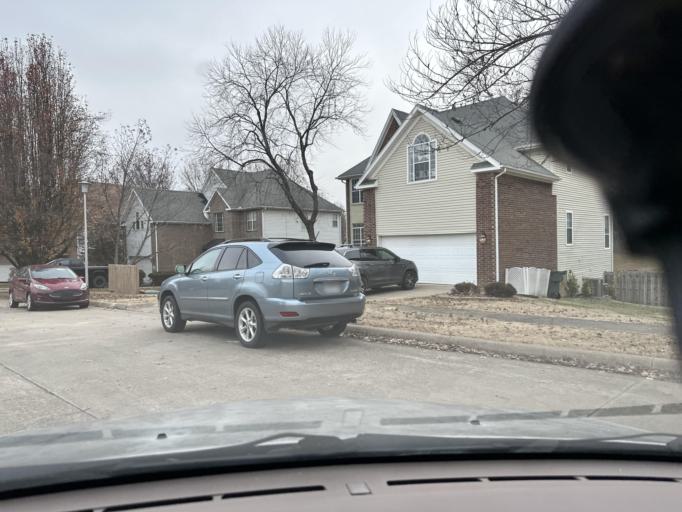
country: US
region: Arkansas
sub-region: Washington County
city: Fayetteville
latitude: 36.0829
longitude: -94.1175
